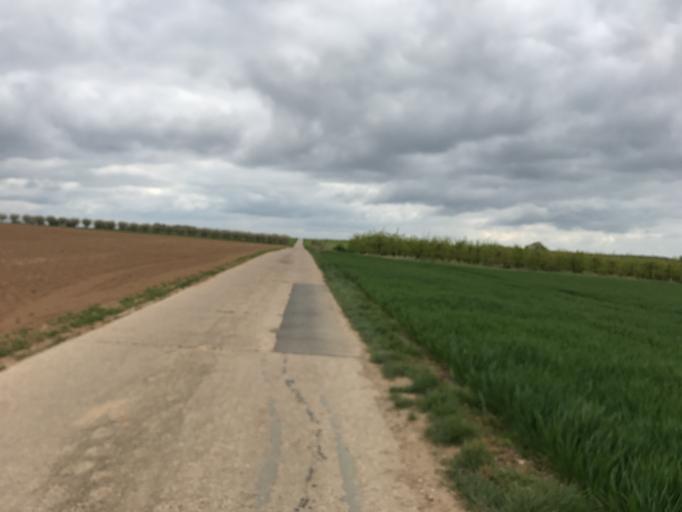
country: DE
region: Rheinland-Pfalz
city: Wackernheim
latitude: 49.9530
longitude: 8.1291
